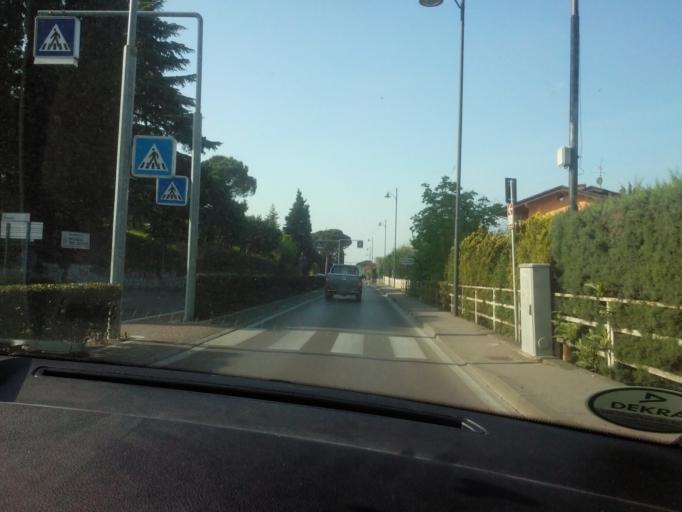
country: IT
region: Lombardy
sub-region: Provincia di Brescia
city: Moniga del Garda
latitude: 45.5264
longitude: 10.5291
